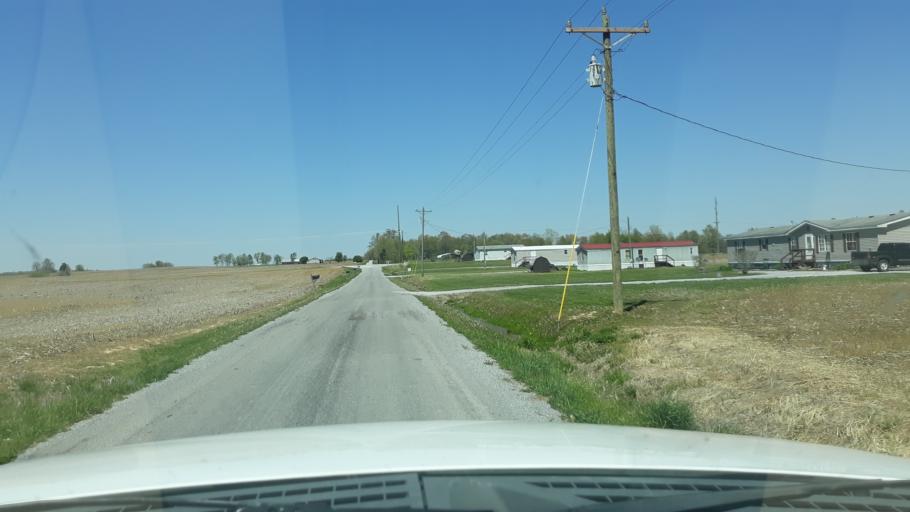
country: US
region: Illinois
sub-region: Saline County
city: Harrisburg
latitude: 37.8757
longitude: -88.6421
